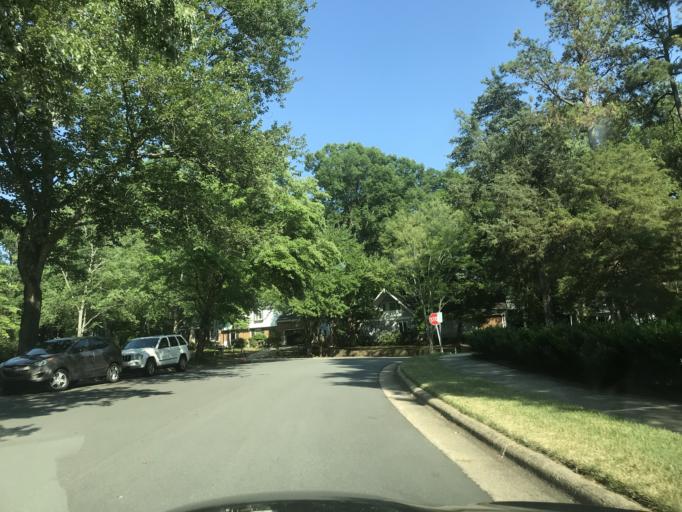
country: US
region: North Carolina
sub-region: Wake County
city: West Raleigh
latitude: 35.8614
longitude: -78.6045
